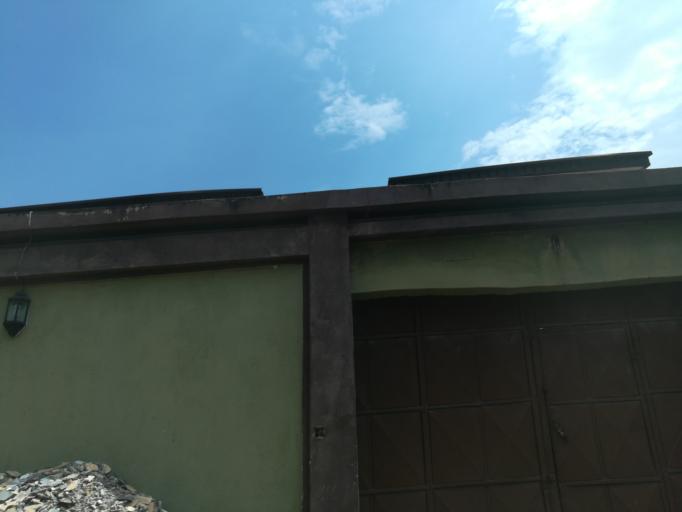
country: NG
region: Lagos
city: Oshodi
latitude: 6.5449
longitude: 3.3225
